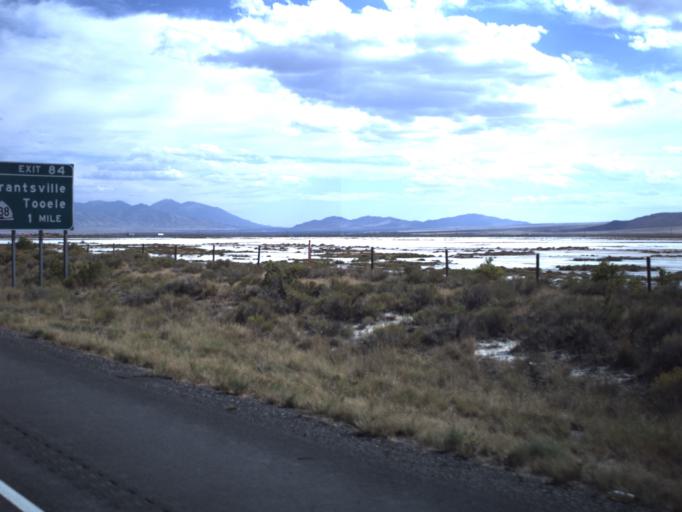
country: US
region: Utah
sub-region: Tooele County
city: Grantsville
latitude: 40.7148
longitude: -112.5429
